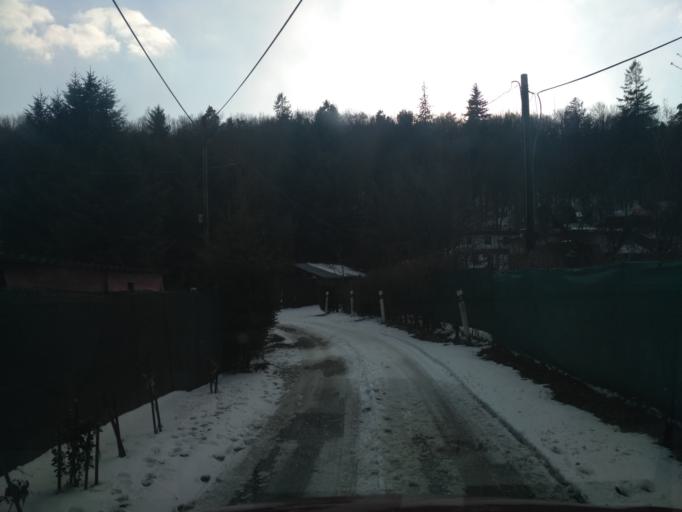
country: SK
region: Kosicky
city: Kosice
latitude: 48.7311
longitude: 21.1615
